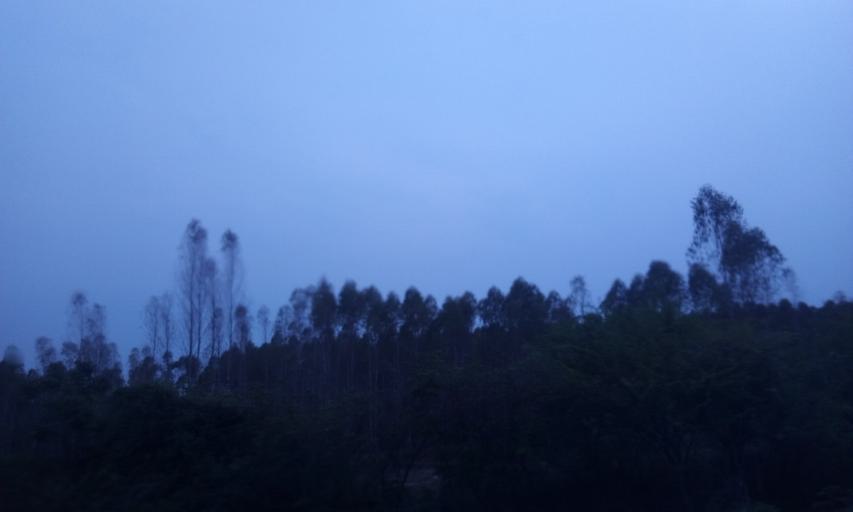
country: TH
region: Chachoengsao
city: Plaeng Yao
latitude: 13.5766
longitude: 101.2440
